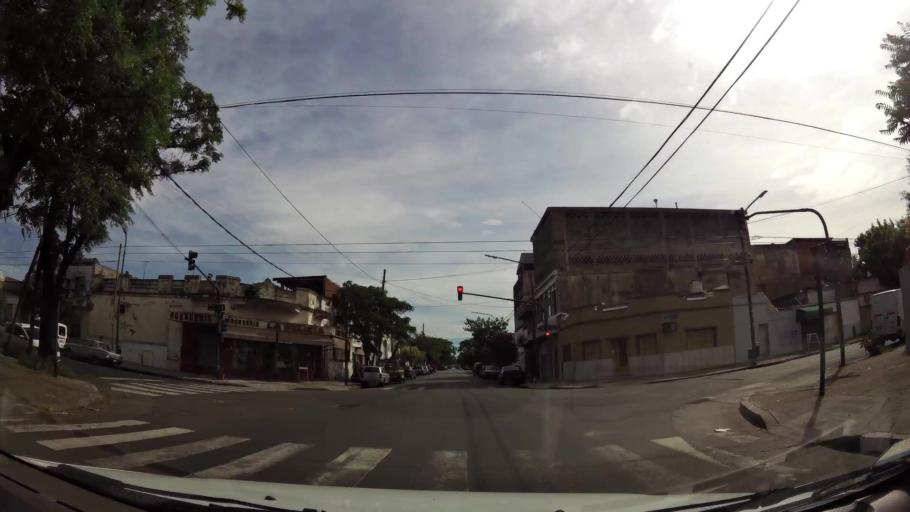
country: AR
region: Buenos Aires F.D.
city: Villa Lugano
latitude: -34.6627
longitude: -58.5063
